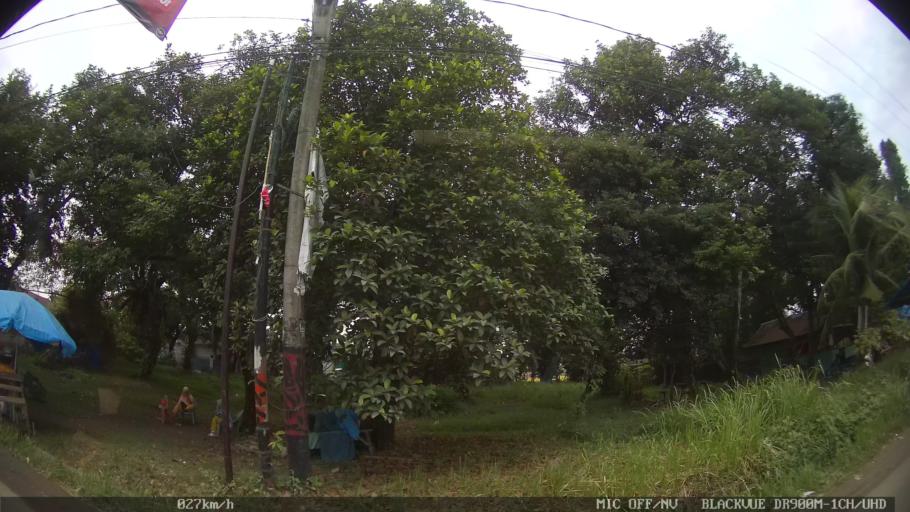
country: ID
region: North Sumatra
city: Sunggal
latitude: 3.6104
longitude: 98.6038
